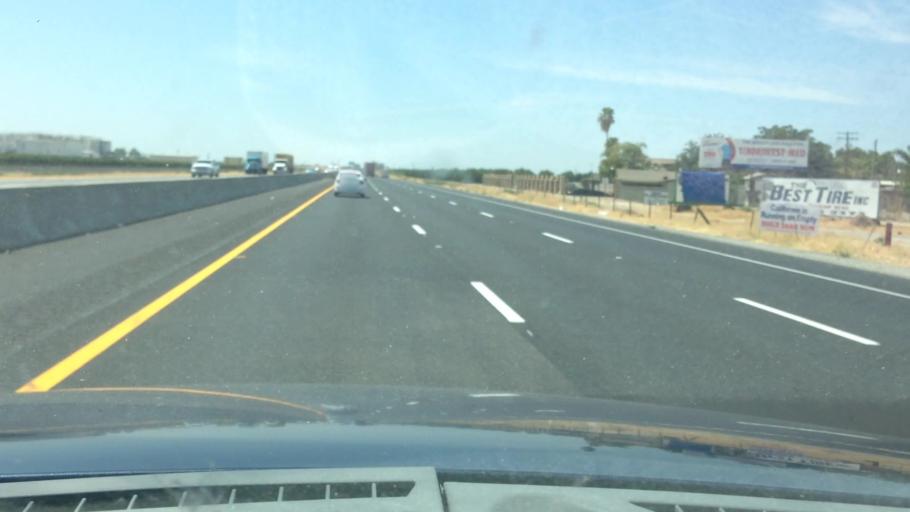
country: US
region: California
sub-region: Kern County
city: McFarland
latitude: 35.7099
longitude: -119.2347
